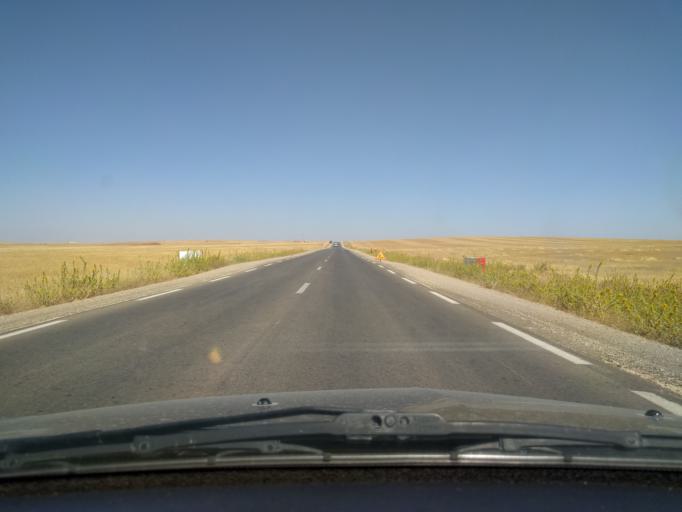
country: DZ
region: Tiaret
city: Frenda
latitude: 34.8818
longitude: 1.1930
